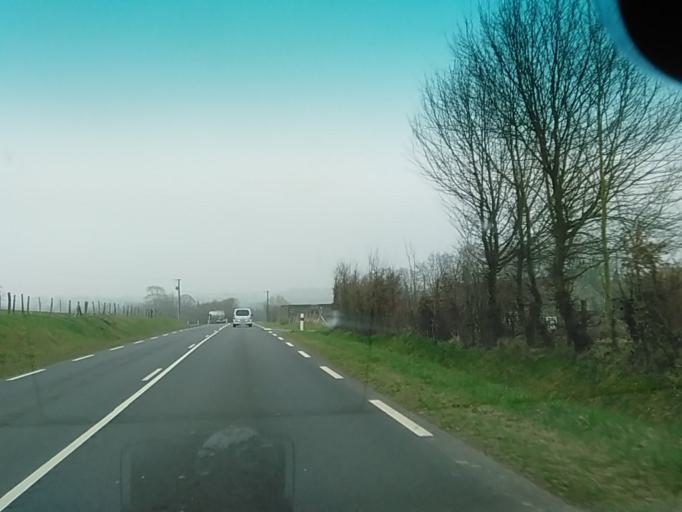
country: FR
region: Lower Normandy
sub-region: Departement de l'Orne
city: Magny-le-Desert
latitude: 48.6175
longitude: -0.2838
